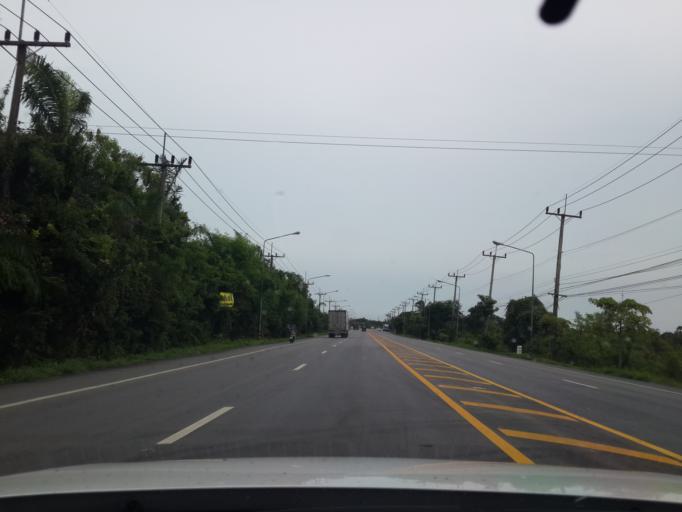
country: TH
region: Pattani
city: Nong Chik
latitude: 6.8285
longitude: 101.1647
